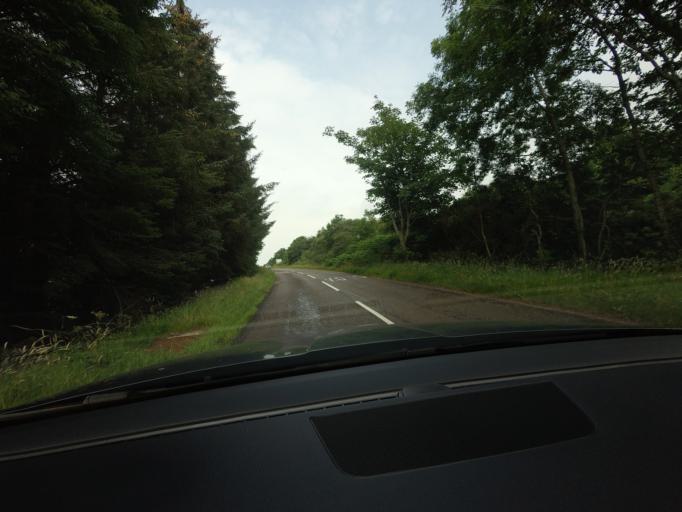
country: GB
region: Scotland
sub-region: Highland
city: Golspie
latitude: 58.4809
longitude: -4.4185
